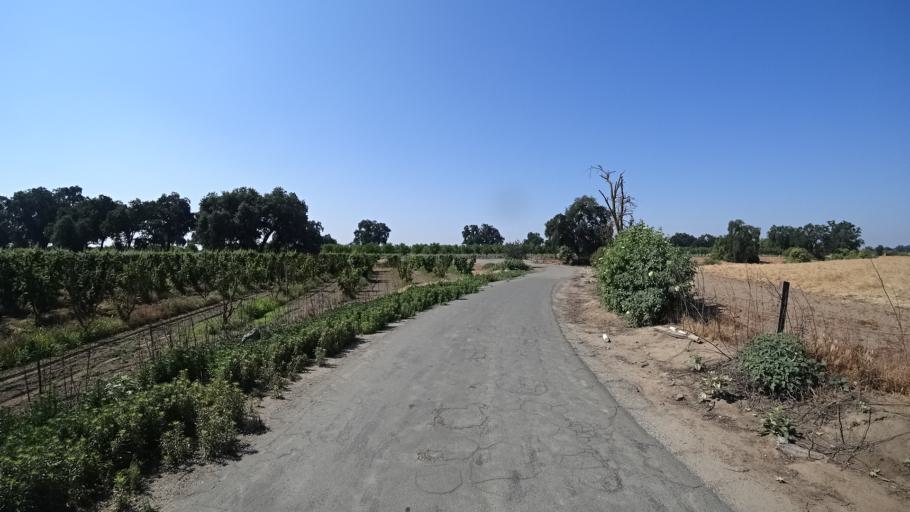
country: US
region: California
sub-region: Fresno County
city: Kingsburg
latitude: 36.4437
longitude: -119.5708
